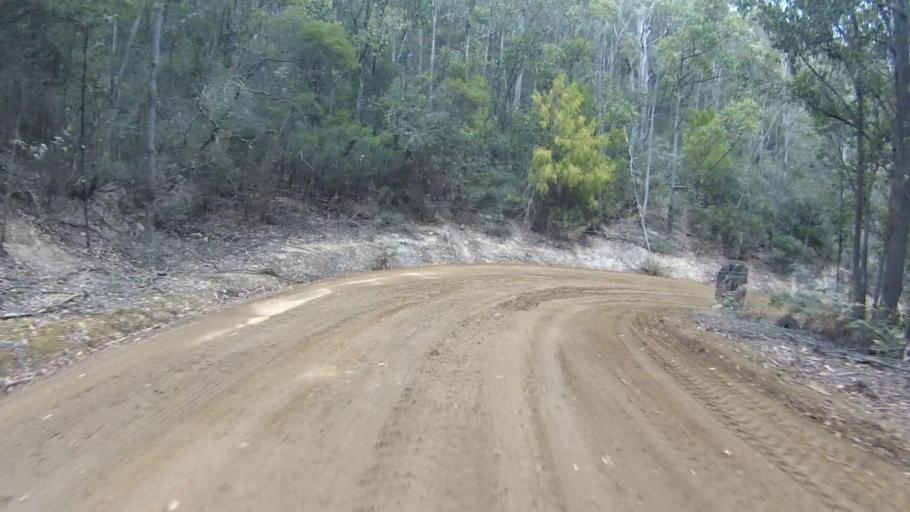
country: AU
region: Tasmania
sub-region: Huon Valley
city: Huonville
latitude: -42.9649
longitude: 147.0481
